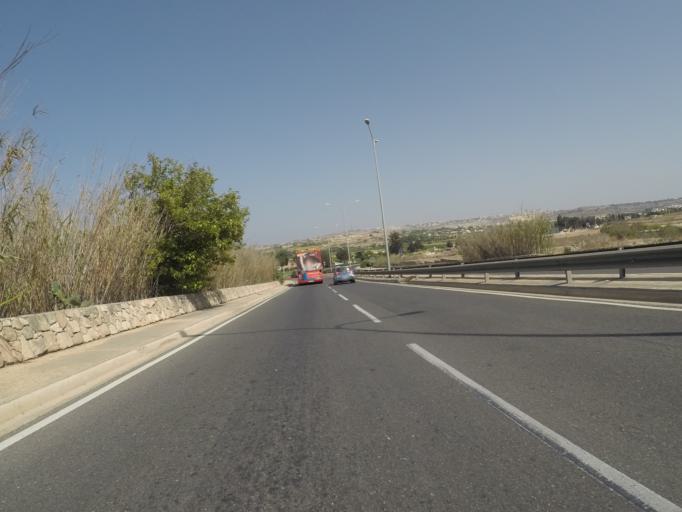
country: MT
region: Saint Paul's Bay
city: San Pawl il-Bahar
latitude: 35.9444
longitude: 14.4098
